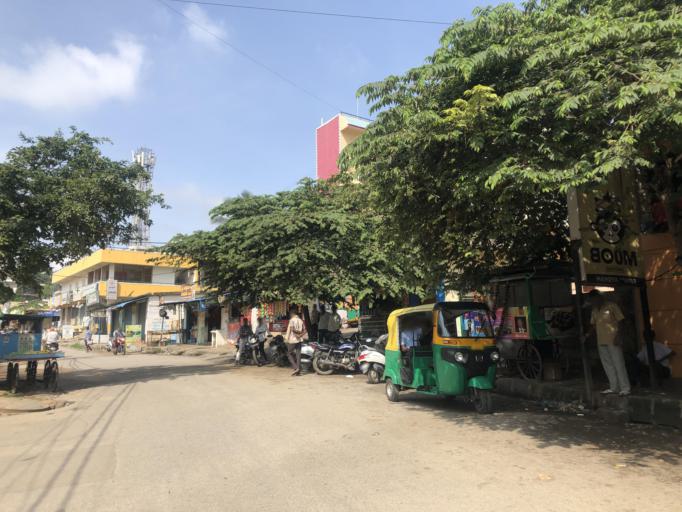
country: IN
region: Karnataka
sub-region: Bangalore Urban
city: Bangalore
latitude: 12.9233
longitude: 77.5296
